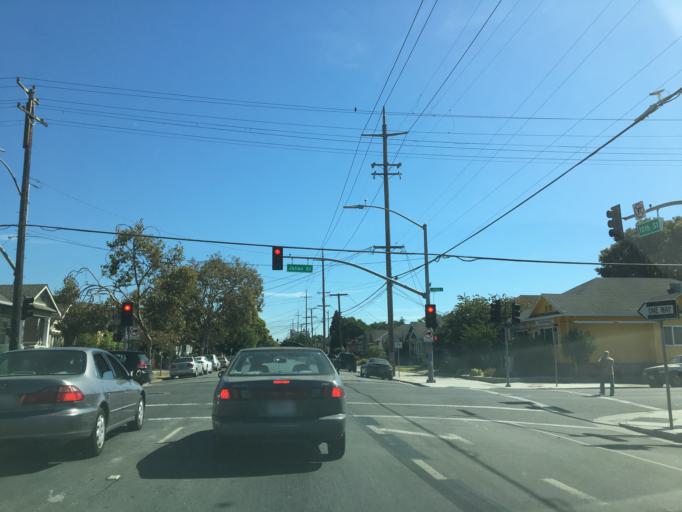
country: US
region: California
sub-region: Santa Clara County
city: San Jose
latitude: 37.3453
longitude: -121.8845
